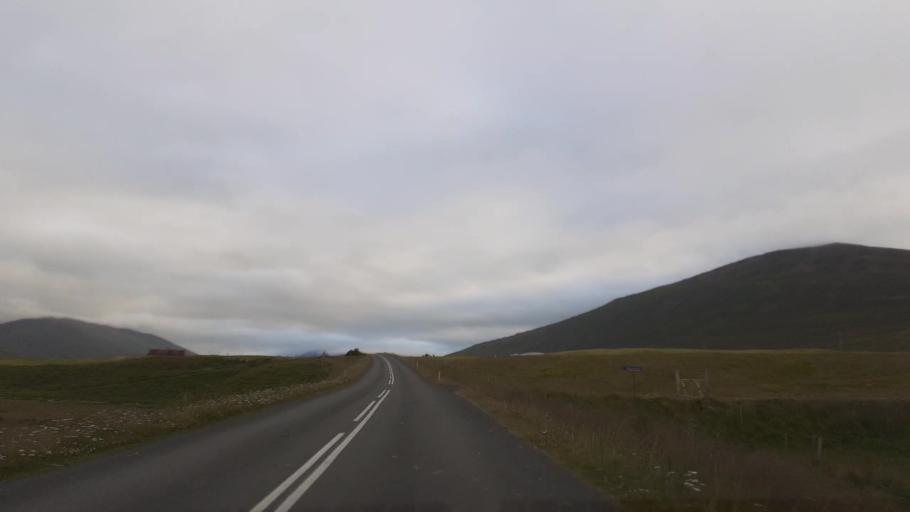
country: IS
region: Northeast
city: Dalvik
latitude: 65.9568
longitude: -18.5492
